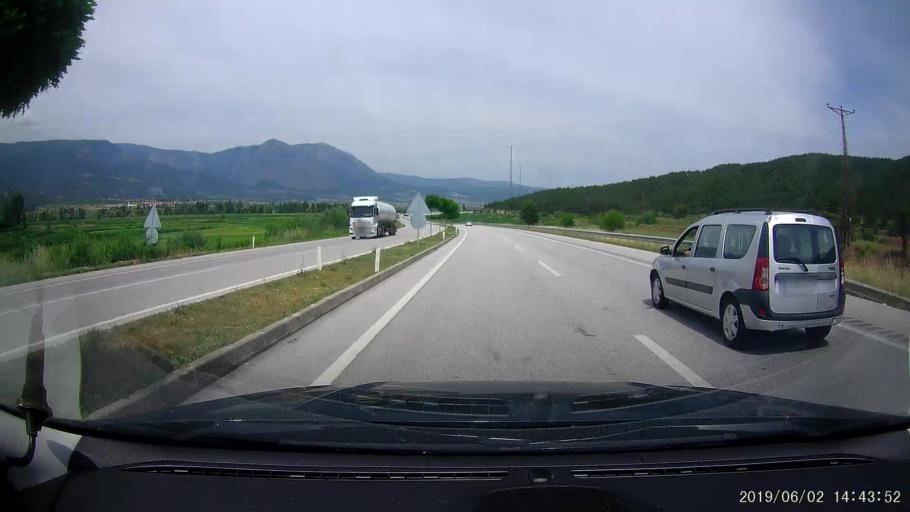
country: TR
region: Corum
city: Hacihamza
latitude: 41.0983
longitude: 34.3994
